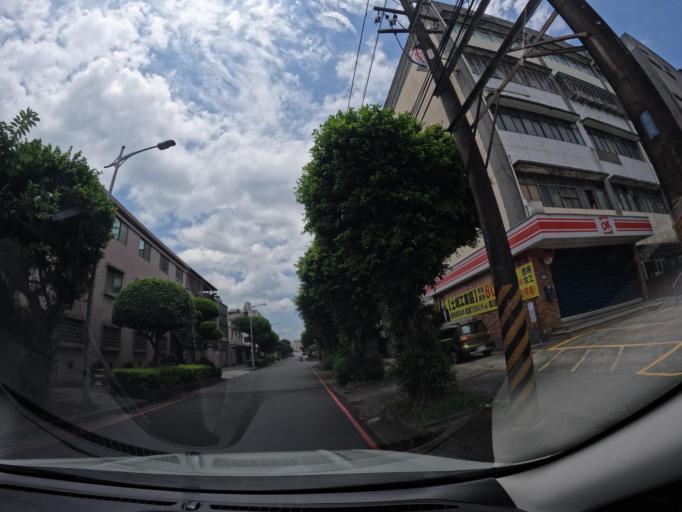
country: TW
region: Taipei
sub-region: Taipei
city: Banqiao
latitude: 24.9703
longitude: 121.4305
